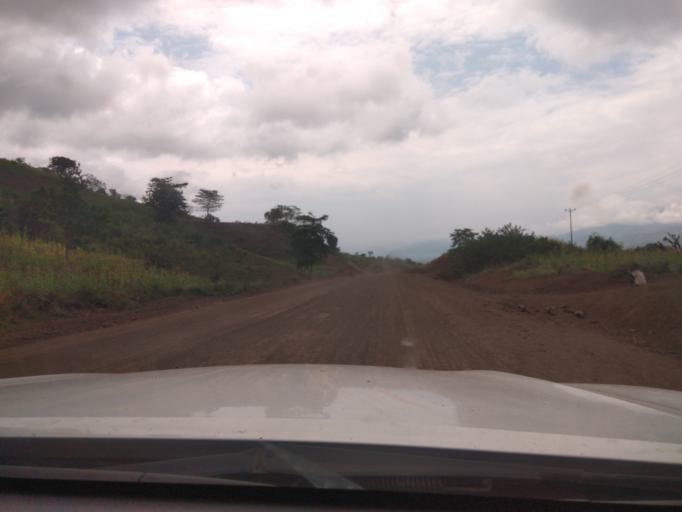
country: ET
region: Southern Nations, Nationalities, and People's Region
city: Felege Neway
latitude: 6.3927
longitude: 37.0709
